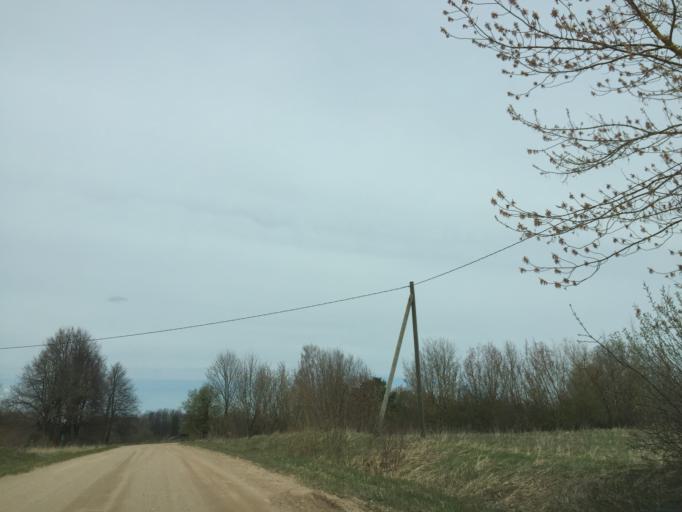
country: LV
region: Ludzas Rajons
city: Ludza
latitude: 56.5192
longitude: 27.5435
